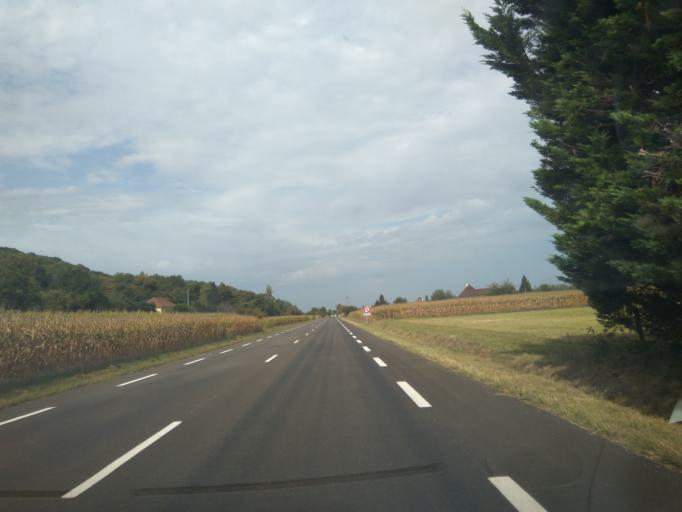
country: FR
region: Aquitaine
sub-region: Departement des Pyrenees-Atlantiques
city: Denguin
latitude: 43.3526
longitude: -0.5287
